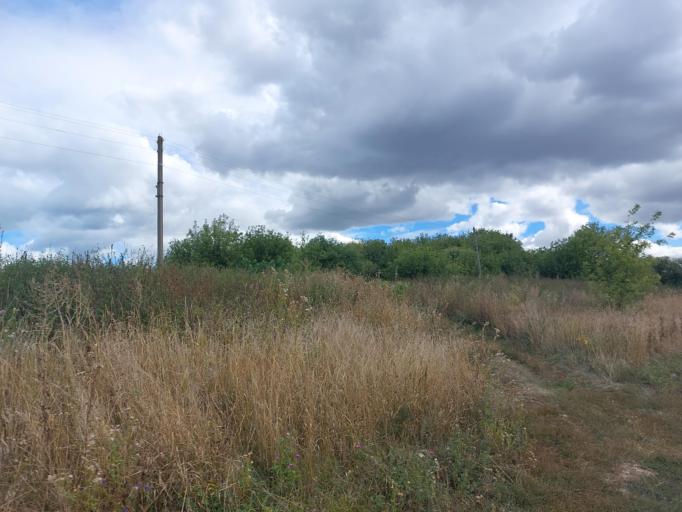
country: RU
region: Lipetsk
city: Terbuny
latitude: 52.2721
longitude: 38.2008
